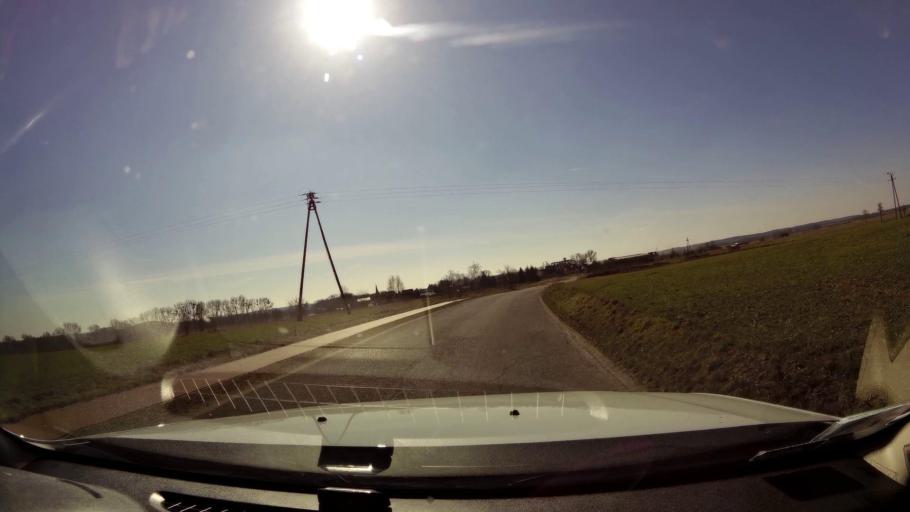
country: PL
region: West Pomeranian Voivodeship
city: Trzcinsko Zdroj
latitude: 52.9776
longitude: 14.6062
